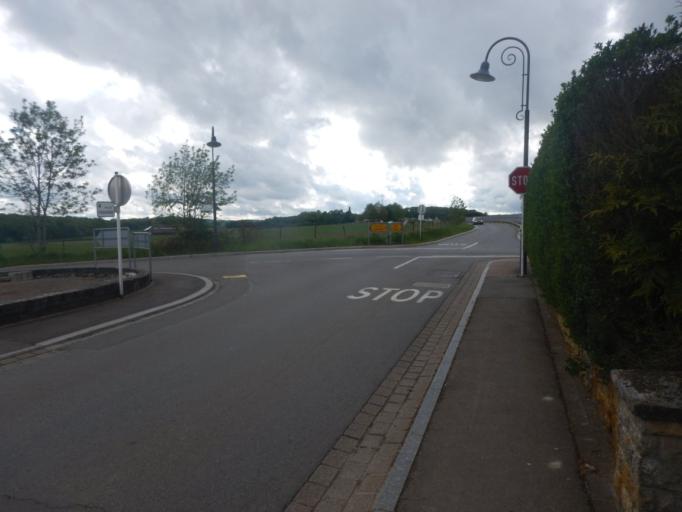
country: LU
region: Luxembourg
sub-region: Canton d'Esch-sur-Alzette
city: Mondercange
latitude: 49.5560
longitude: 5.9795
